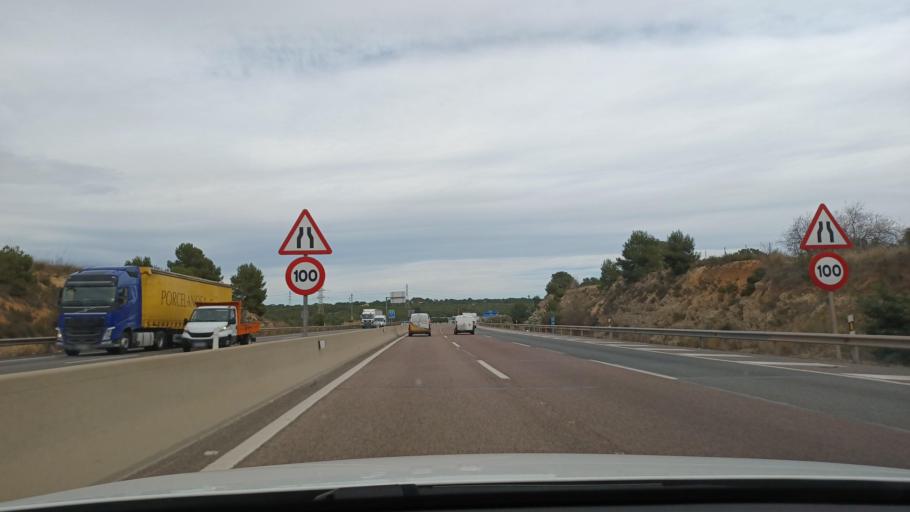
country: ES
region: Valencia
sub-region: Provincia de Valencia
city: Manises
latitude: 39.5097
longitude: -0.5054
